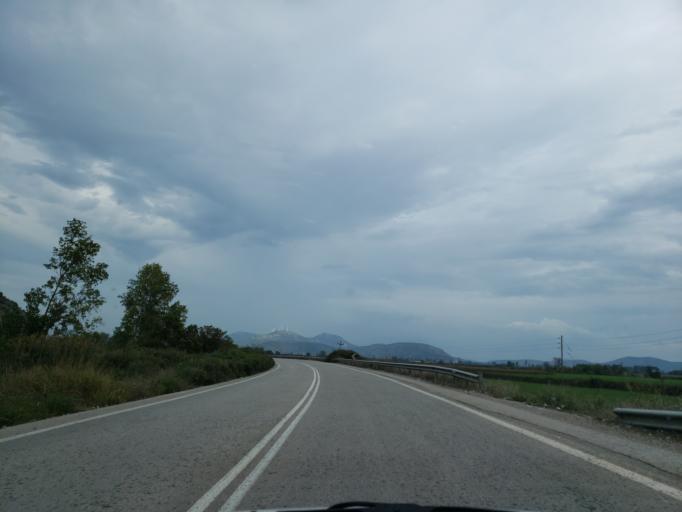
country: GR
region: Central Greece
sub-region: Nomos Voiotias
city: Akraifnia
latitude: 38.4755
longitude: 23.1137
